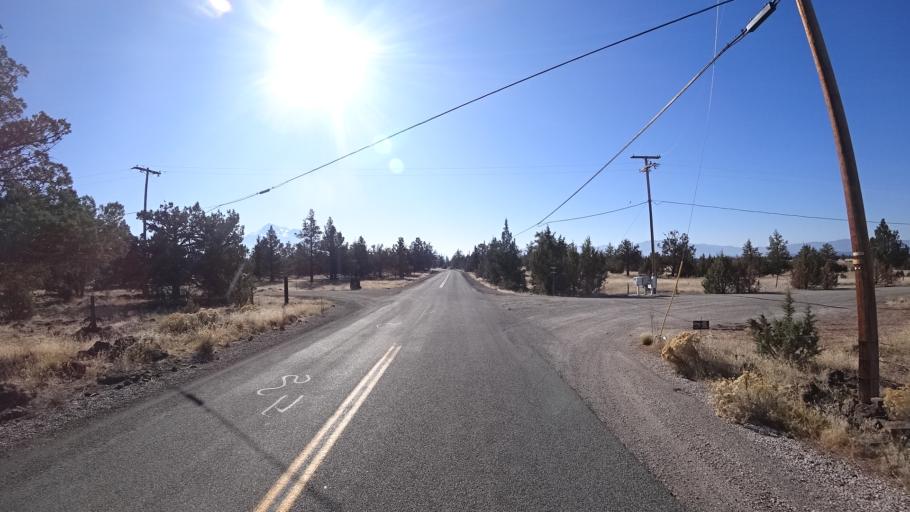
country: US
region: California
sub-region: Siskiyou County
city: Montague
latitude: 41.6496
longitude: -122.3598
